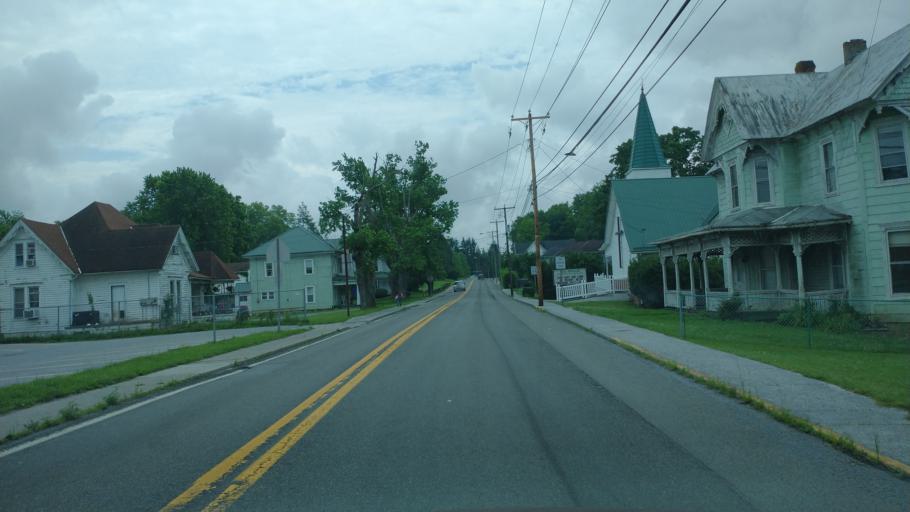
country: US
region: West Virginia
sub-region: Mercer County
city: Athens
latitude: 37.4214
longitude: -81.0157
